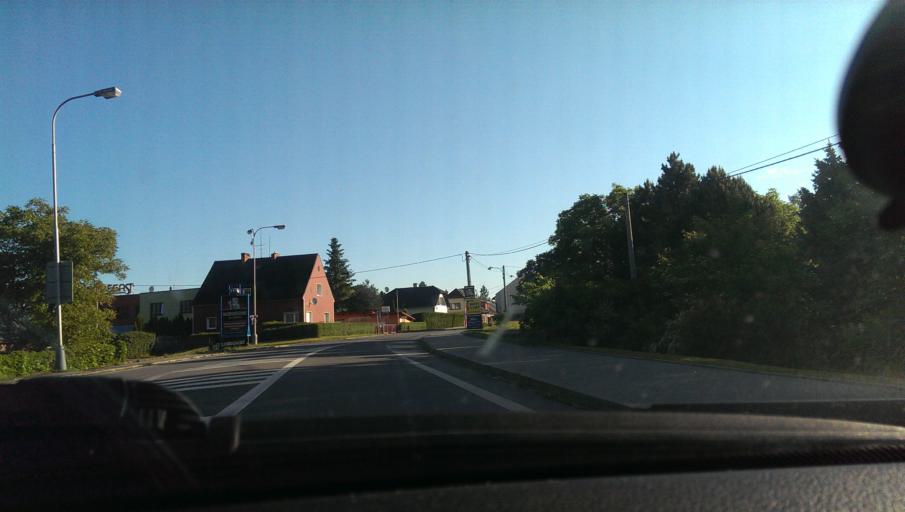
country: CZ
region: Moravskoslezsky
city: Frenstat pod Radhostem
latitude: 49.5491
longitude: 18.2145
